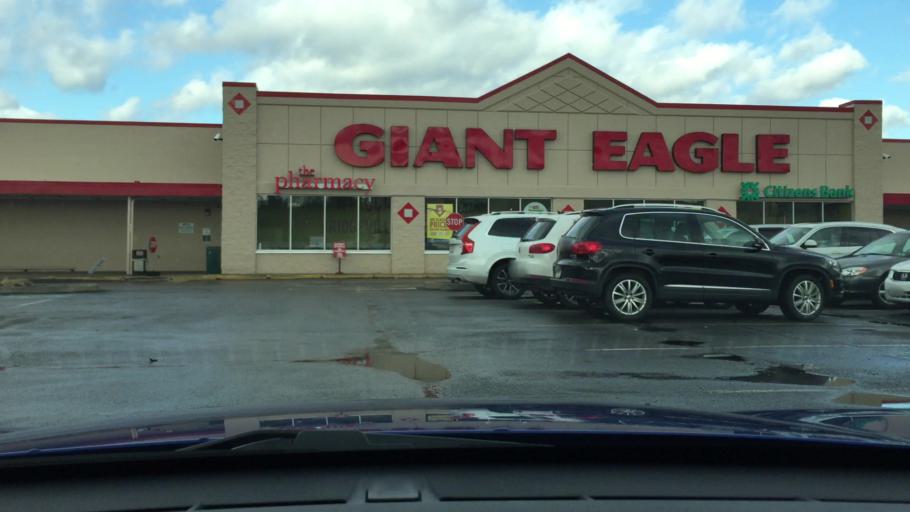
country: US
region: Pennsylvania
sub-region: Allegheny County
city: Bridgeville
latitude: 40.3669
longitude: -80.1092
